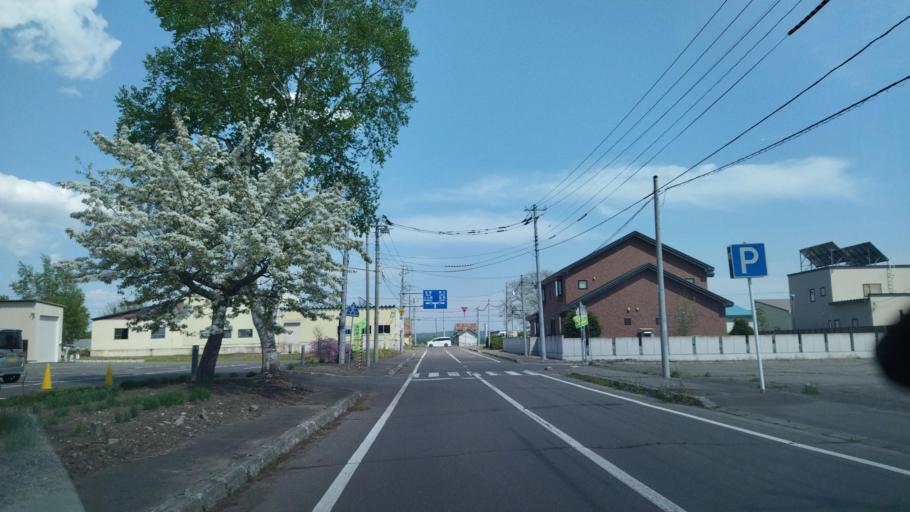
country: JP
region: Hokkaido
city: Otofuke
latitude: 43.0991
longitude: 143.2286
